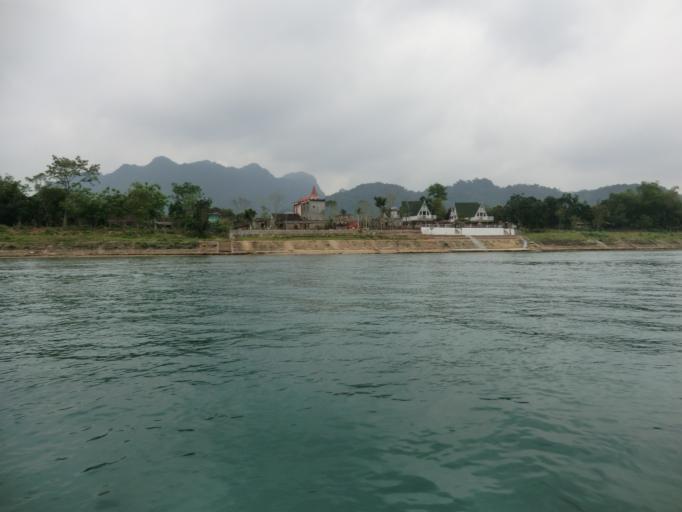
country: VN
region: Quang Binh
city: Ba Don
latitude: 17.6003
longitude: 106.2915
